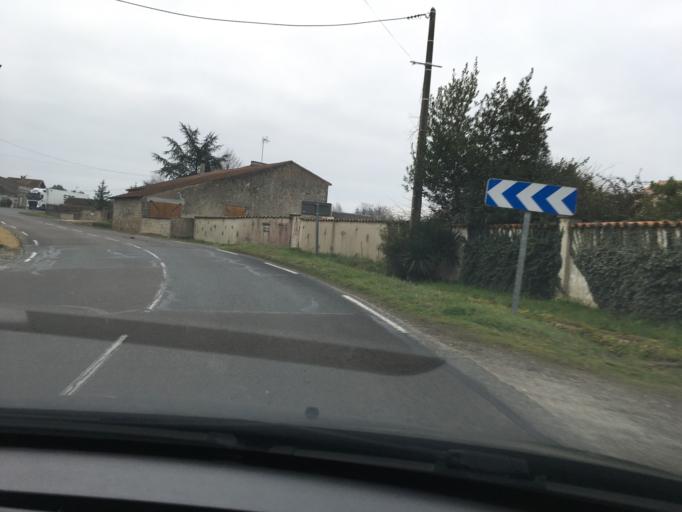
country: FR
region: Aquitaine
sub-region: Departement de la Gironde
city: Saint-Ciers-sur-Gironde
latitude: 45.2739
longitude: -0.5947
